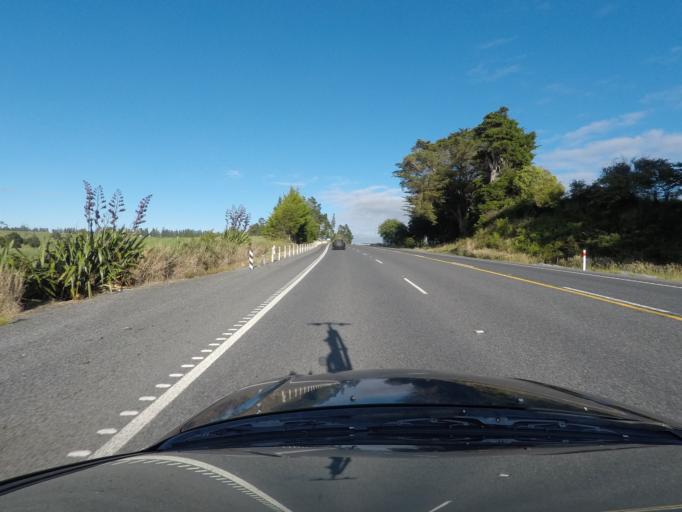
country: NZ
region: Northland
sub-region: Far North District
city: Kawakawa
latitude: -35.5119
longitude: 174.1826
